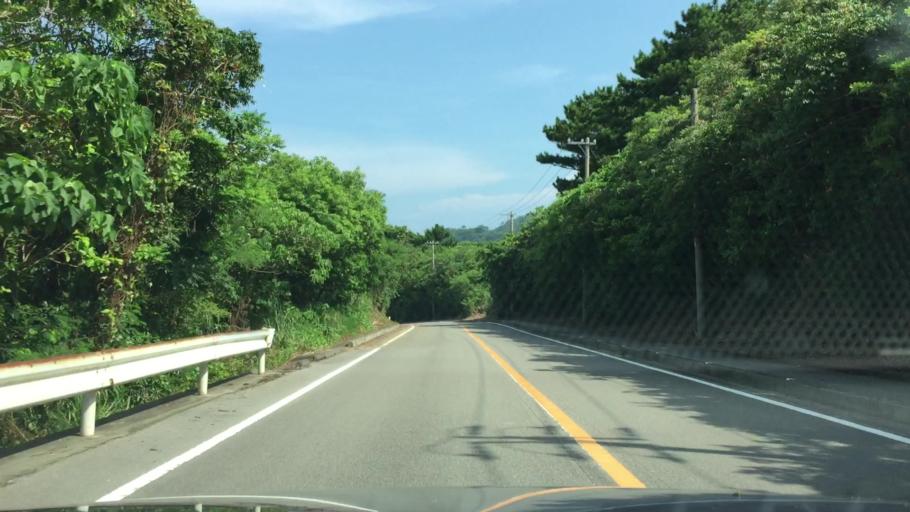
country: JP
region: Okinawa
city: Ishigaki
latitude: 24.5108
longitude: 124.2676
